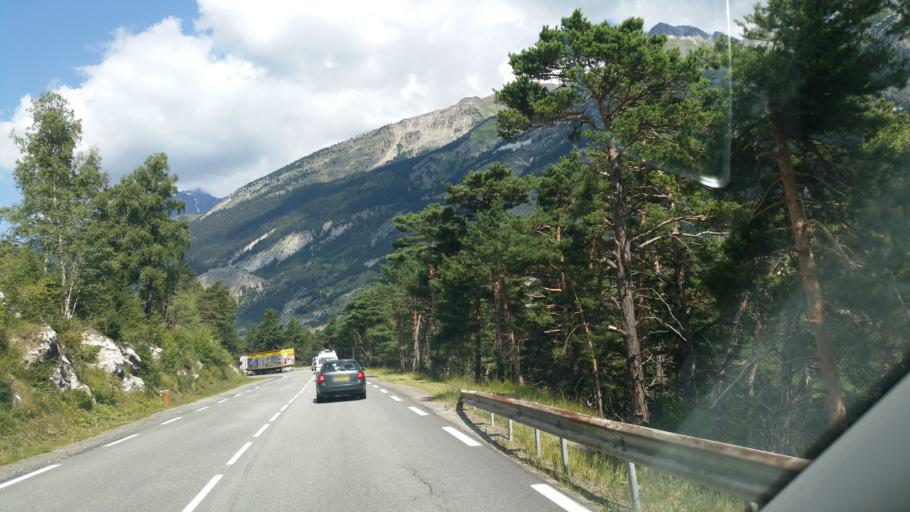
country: FR
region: Rhone-Alpes
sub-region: Departement de la Savoie
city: Modane
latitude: 45.2102
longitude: 6.7252
